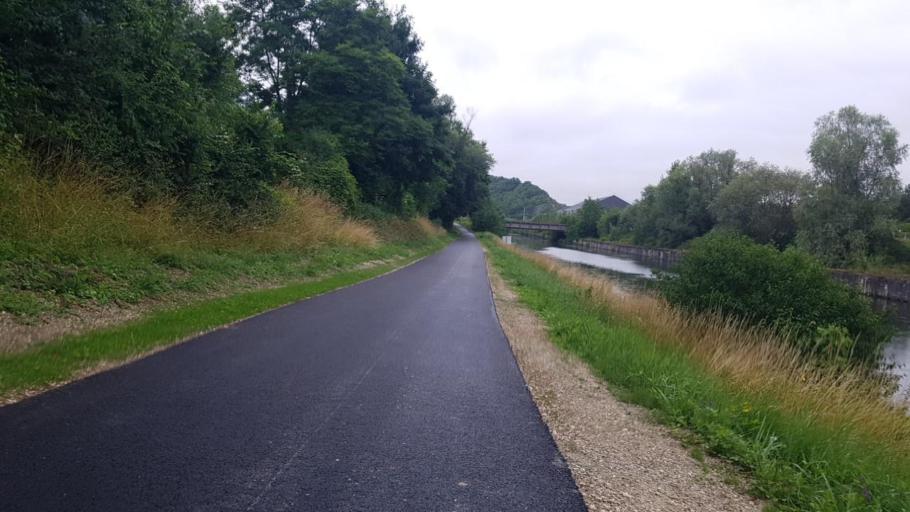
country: FR
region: Champagne-Ardenne
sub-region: Departement de la Marne
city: Vitry-le-Francois
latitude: 48.7635
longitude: 4.5613
